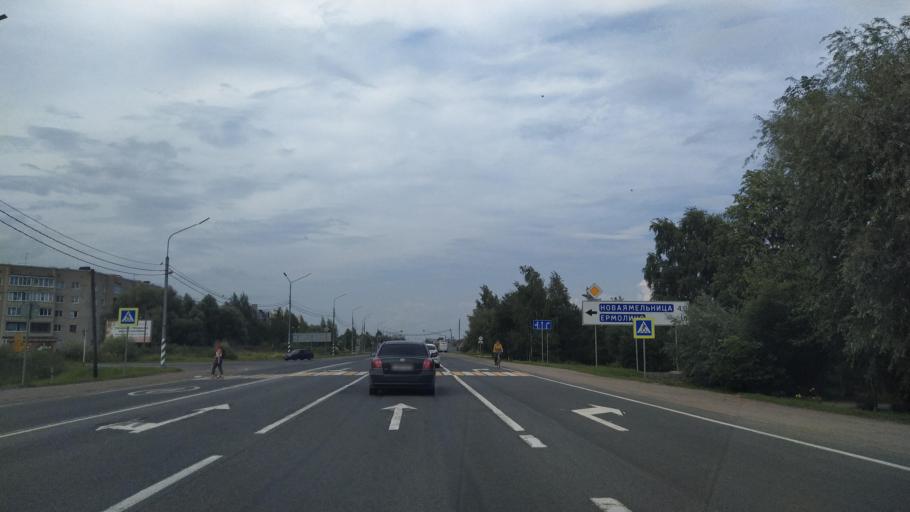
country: RU
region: Novgorod
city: Pankovka
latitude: 58.4908
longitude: 31.2028
